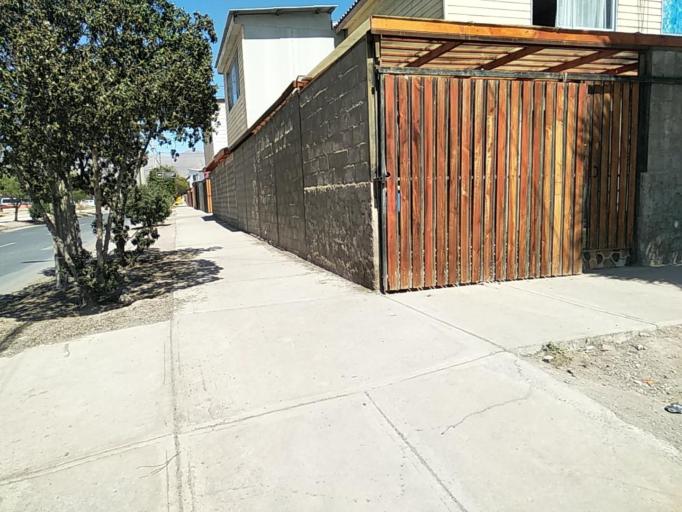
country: CL
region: Atacama
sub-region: Provincia de Copiapo
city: Copiapo
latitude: -27.4080
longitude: -70.2830
